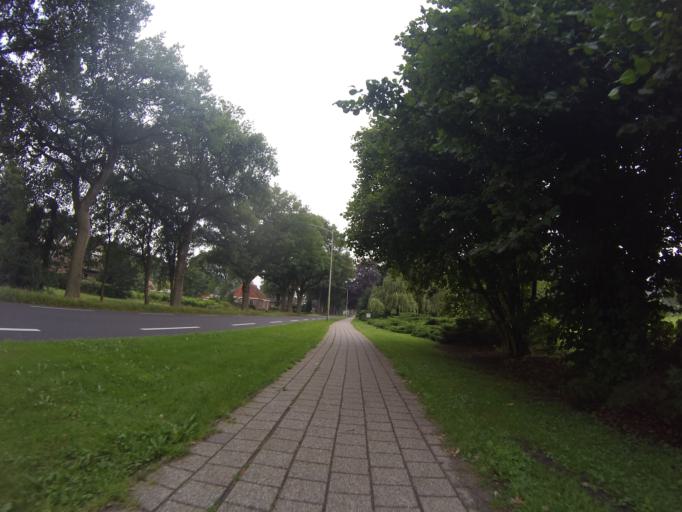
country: NL
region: Drenthe
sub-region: Gemeente Emmen
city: Emmen
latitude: 52.8105
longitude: 6.9075
